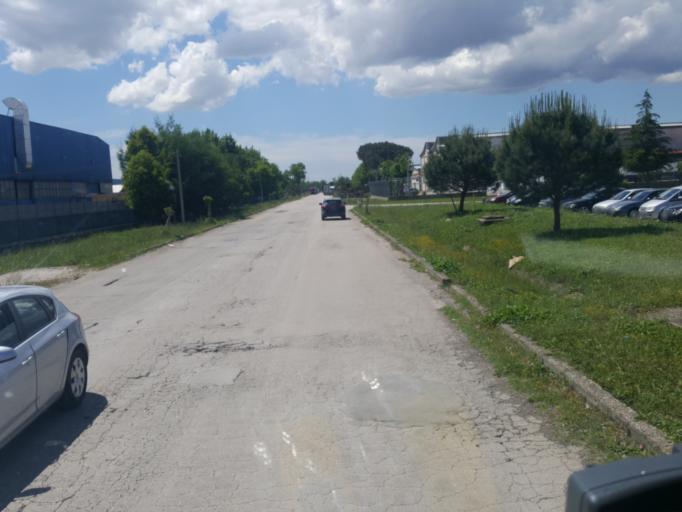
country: IT
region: Campania
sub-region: Provincia di Napoli
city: Pascarola
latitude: 40.9866
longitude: 14.3018
